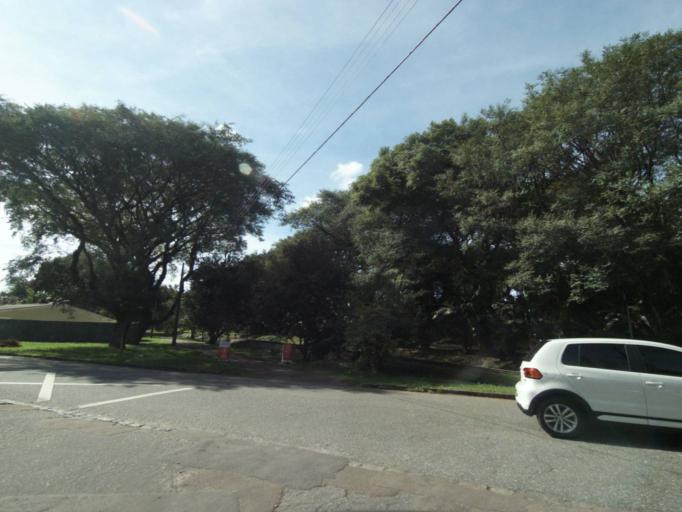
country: BR
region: Parana
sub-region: Curitiba
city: Curitiba
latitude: -25.4212
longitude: -49.2459
